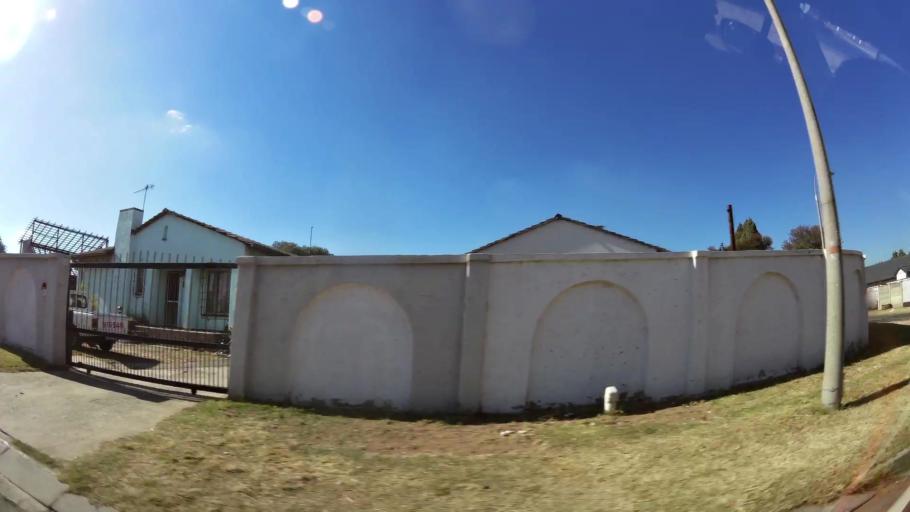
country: ZA
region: Gauteng
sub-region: City of Johannesburg Metropolitan Municipality
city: Roodepoort
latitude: -26.1462
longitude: 27.8246
